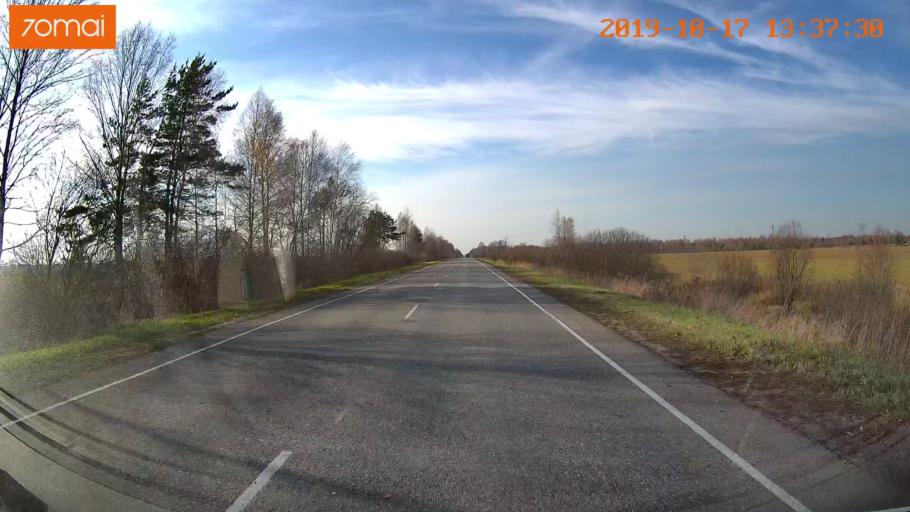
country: RU
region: Rjazan
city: Tuma
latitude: 55.1417
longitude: 40.6376
